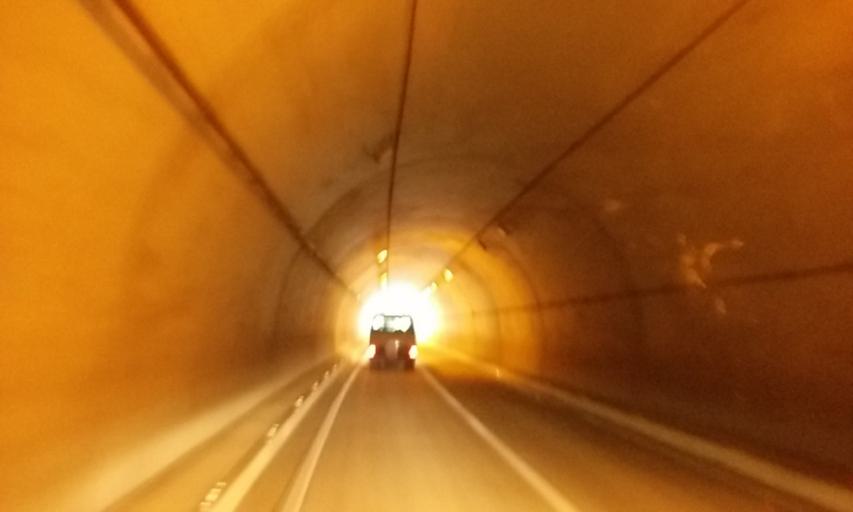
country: JP
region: Ehime
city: Niihama
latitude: 33.8757
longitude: 133.2950
